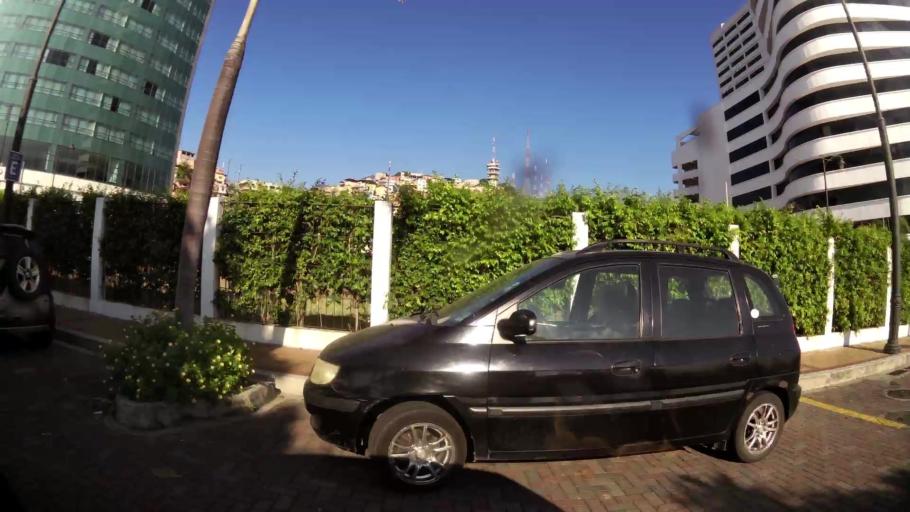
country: EC
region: Guayas
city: Eloy Alfaro
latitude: -2.1787
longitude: -79.8758
